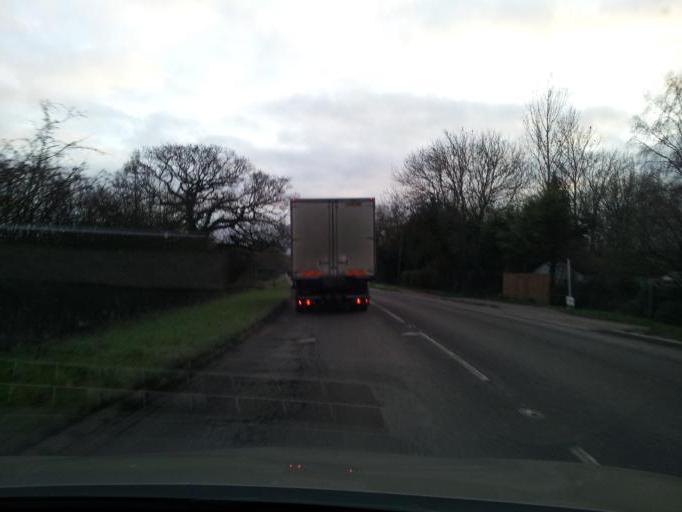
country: GB
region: England
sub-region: Cambridgeshire
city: Comberton
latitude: 52.2155
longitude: 0.0406
